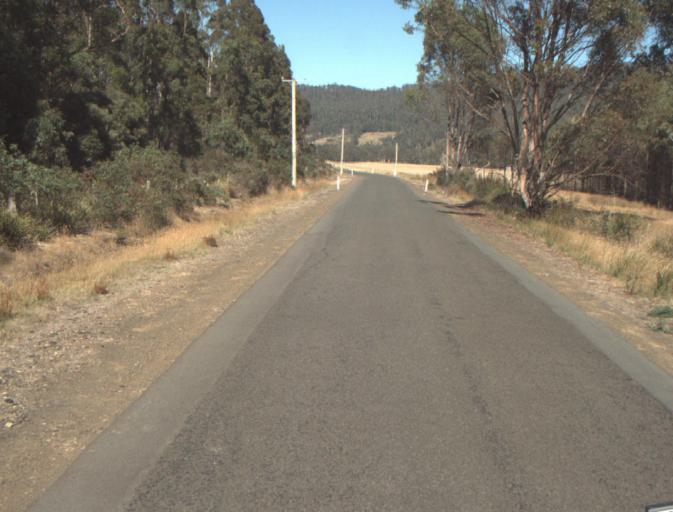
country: AU
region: Tasmania
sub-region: Launceston
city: Newstead
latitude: -41.3272
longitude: 147.3135
